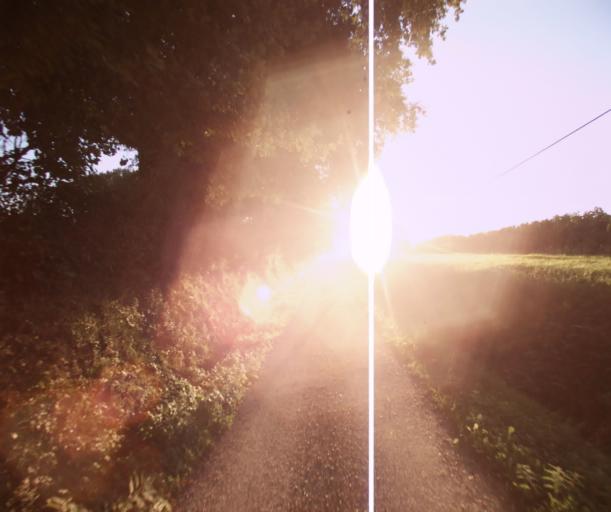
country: FR
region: Midi-Pyrenees
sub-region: Departement du Gers
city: Eauze
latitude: 43.8940
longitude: 0.0682
